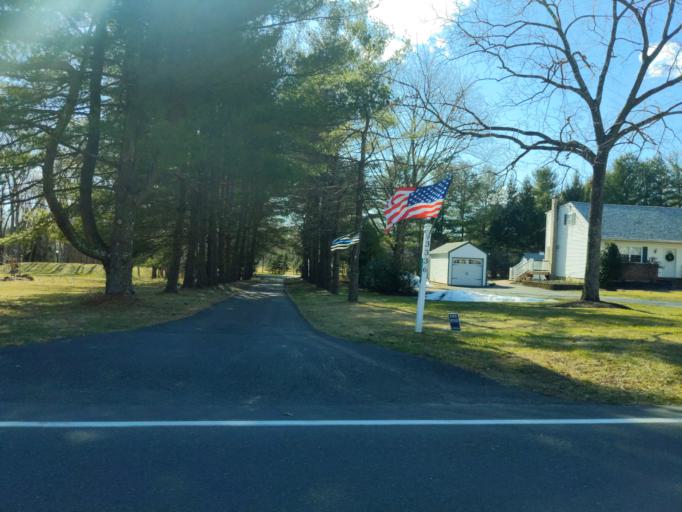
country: US
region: Pennsylvania
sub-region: Montgomery County
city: Red Hill
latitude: 40.3683
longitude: -75.4583
